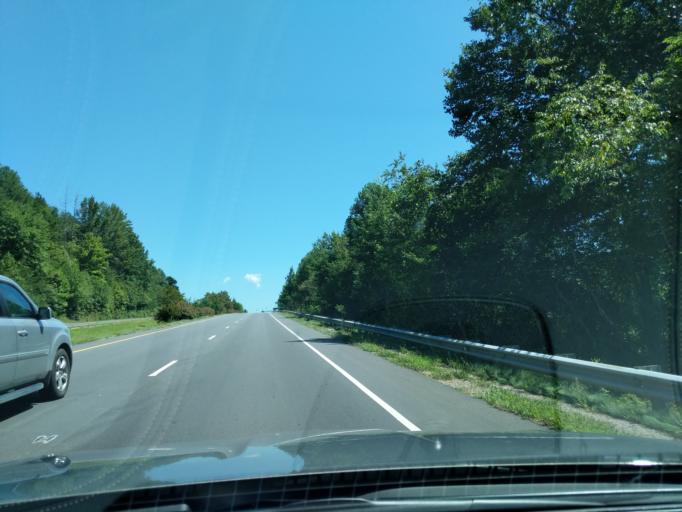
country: US
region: North Carolina
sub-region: Macon County
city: Franklin
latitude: 35.1648
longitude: -83.4122
